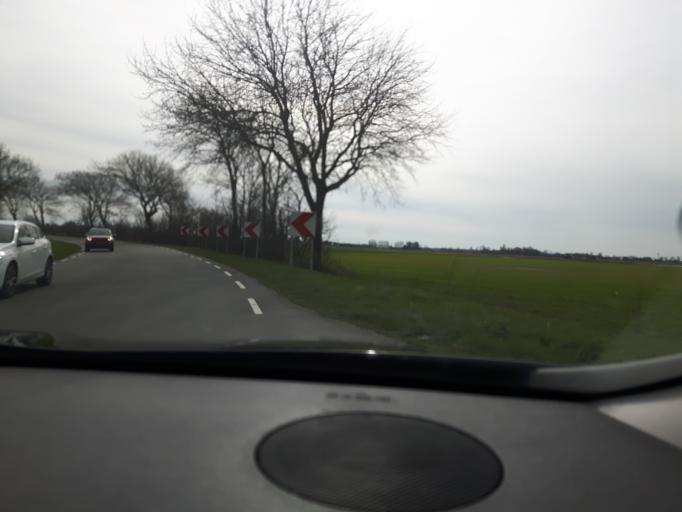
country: NL
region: Zeeland
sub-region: Gemeente Middelburg
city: Middelburg
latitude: 51.5186
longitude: 3.5993
